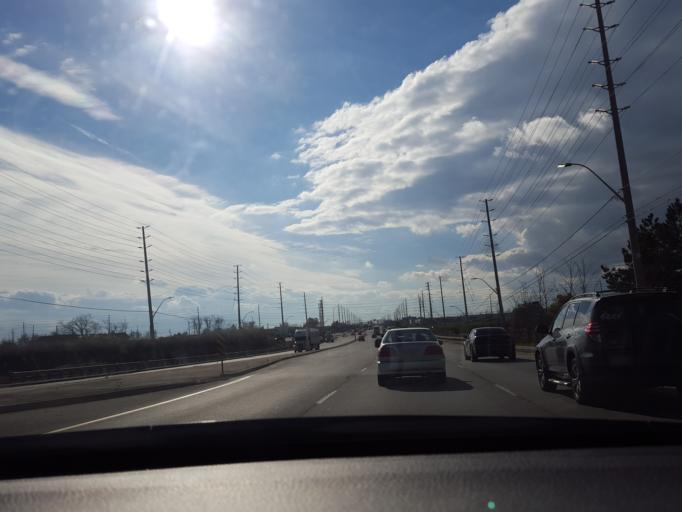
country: CA
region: Ontario
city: Brampton
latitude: 43.6778
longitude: -79.6715
